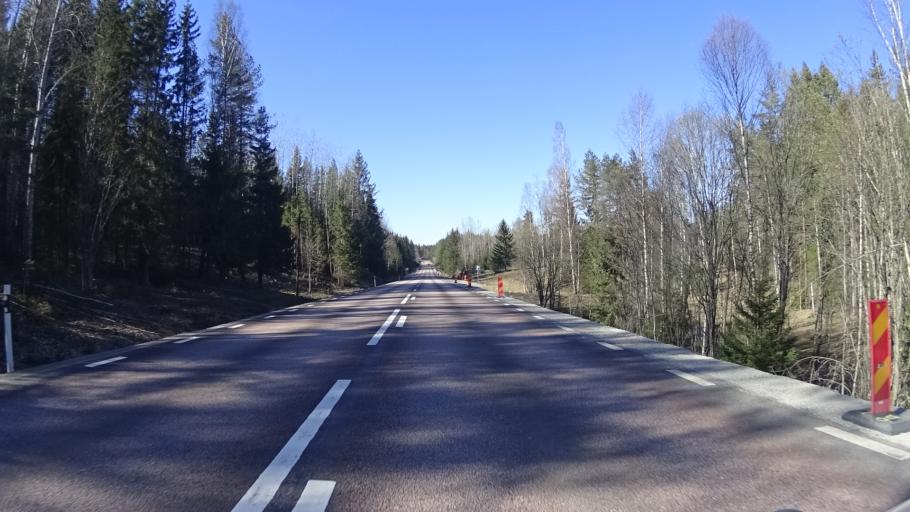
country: SE
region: Vaermland
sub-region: Karlstads Kommun
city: Edsvalla
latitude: 59.5977
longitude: 13.0044
